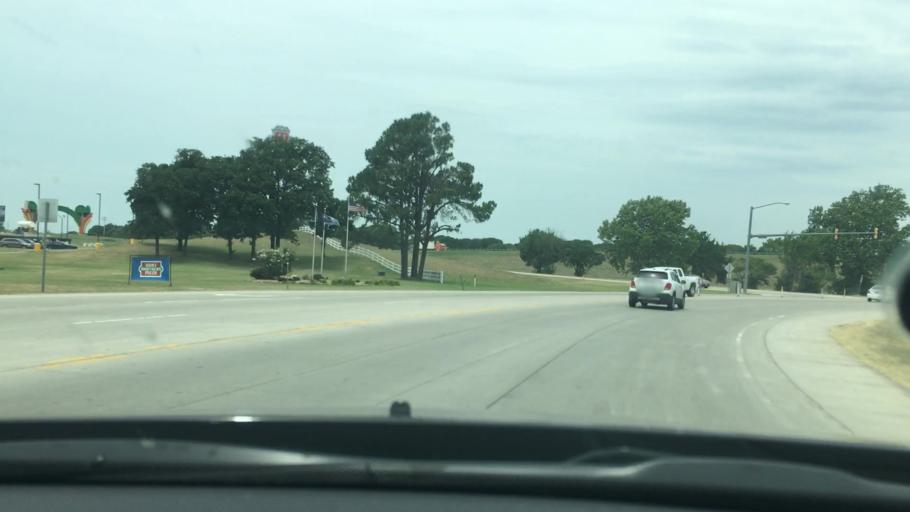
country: US
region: Texas
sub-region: Cooke County
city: Gainesville
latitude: 33.7369
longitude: -97.1437
